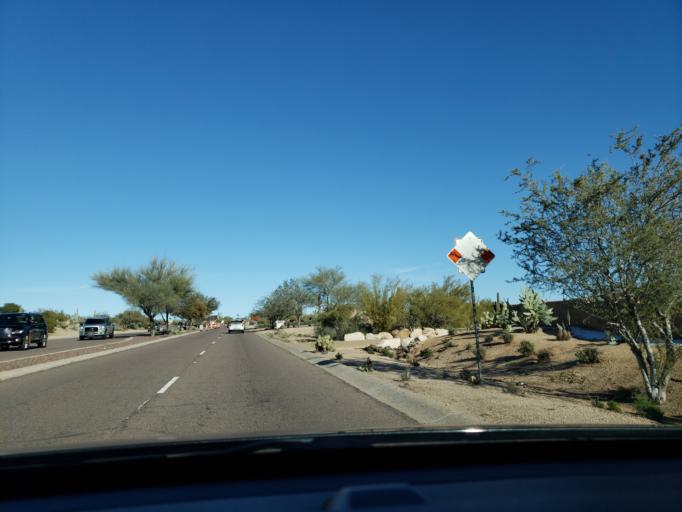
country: US
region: Arizona
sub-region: Maricopa County
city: Carefree
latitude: 33.8185
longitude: -111.8897
